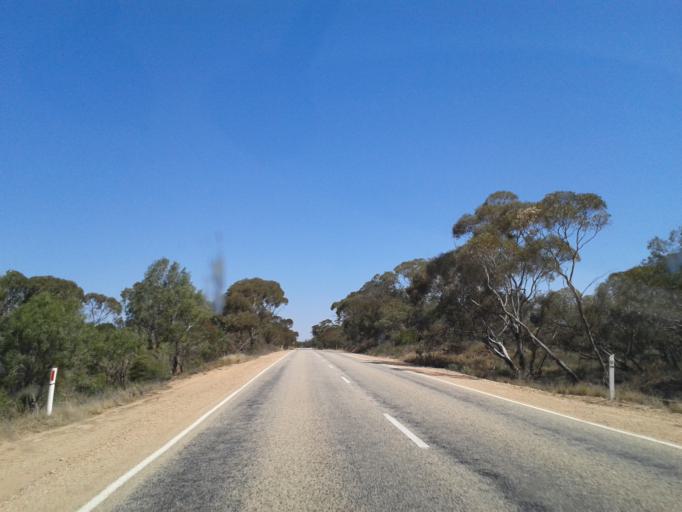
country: AU
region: Victoria
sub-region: Swan Hill
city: Swan Hill
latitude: -34.8358
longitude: 143.2627
